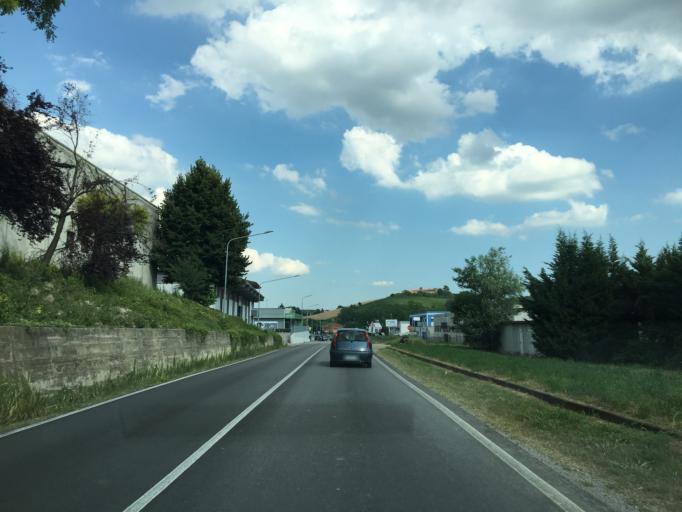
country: IT
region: Piedmont
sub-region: Provincia di Cuneo
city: Piobesi d'Alba
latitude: 44.7287
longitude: 7.9949
